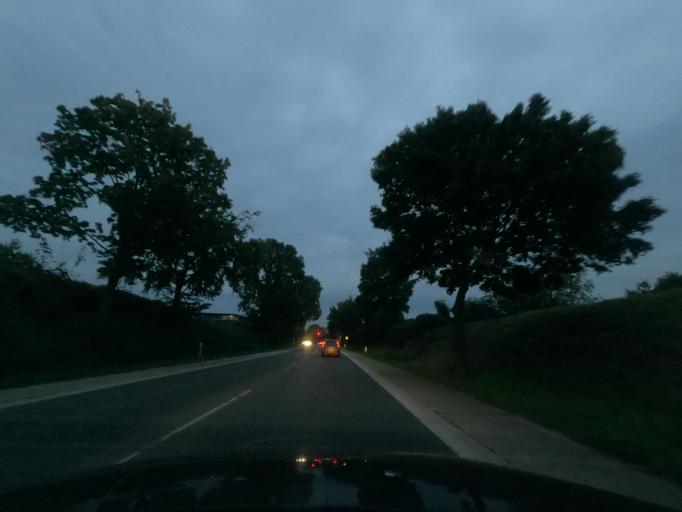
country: DE
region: North Rhine-Westphalia
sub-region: Regierungsbezirk Dusseldorf
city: Wesel
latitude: 51.6767
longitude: 6.6271
